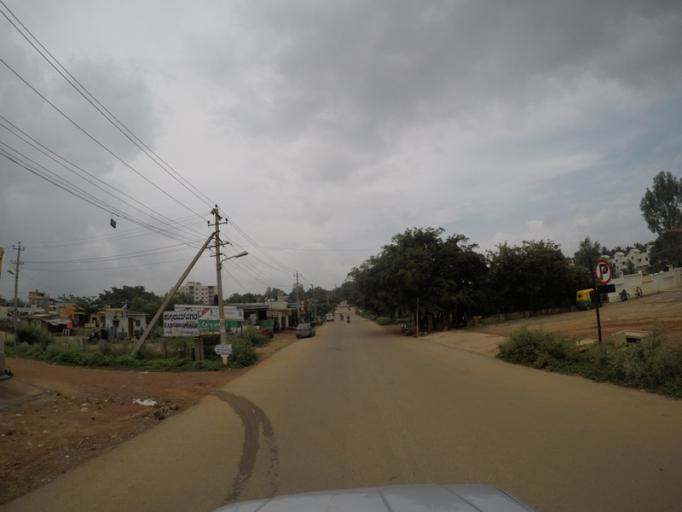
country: IN
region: Karnataka
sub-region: Bangalore Urban
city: Yelahanka
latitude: 13.0910
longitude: 77.5370
